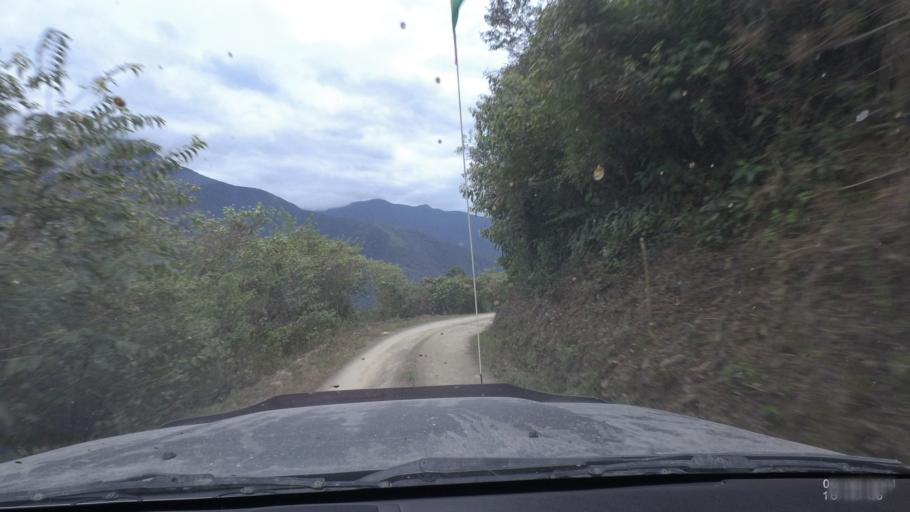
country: BO
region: La Paz
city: Quime
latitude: -16.5406
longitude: -66.7567
